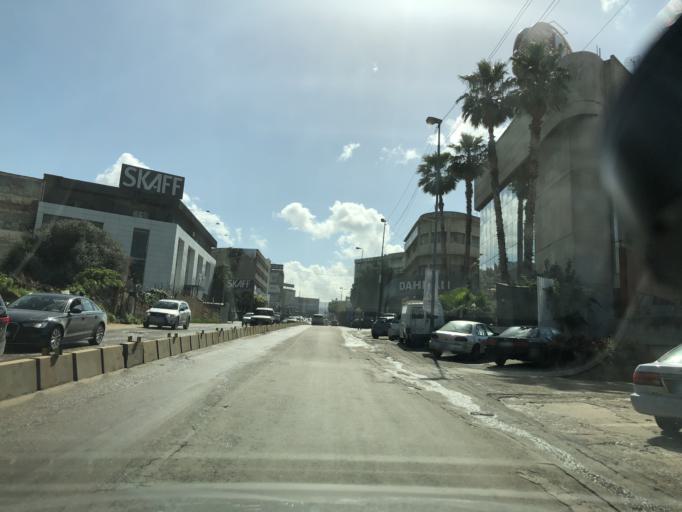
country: LB
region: Mont-Liban
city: Jdaidet el Matn
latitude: 33.8667
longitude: 35.5449
